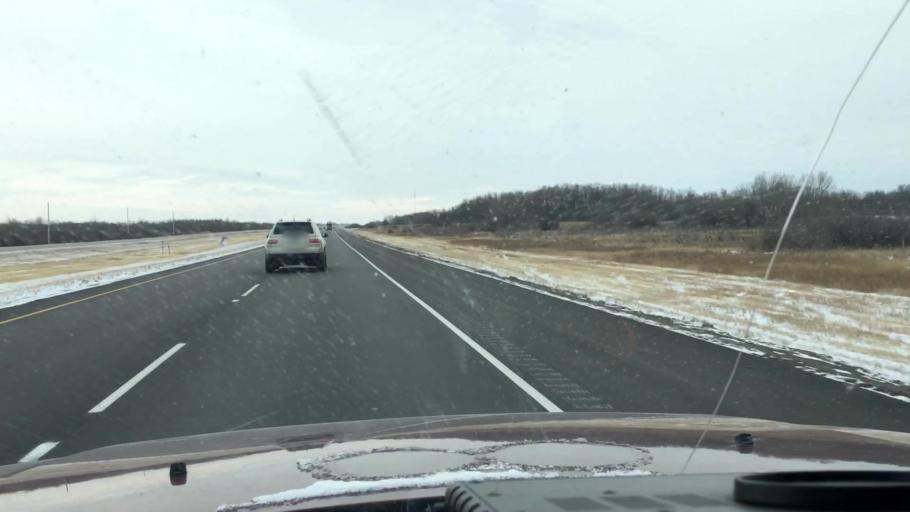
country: CA
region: Saskatchewan
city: Saskatoon
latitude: 51.8808
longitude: -106.5125
